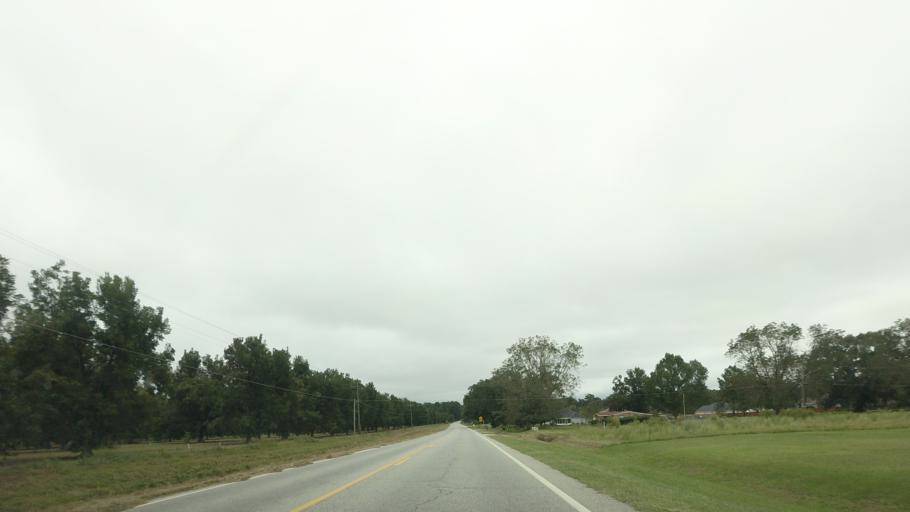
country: US
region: Georgia
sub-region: Berrien County
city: Ray City
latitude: 31.0437
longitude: -83.1977
